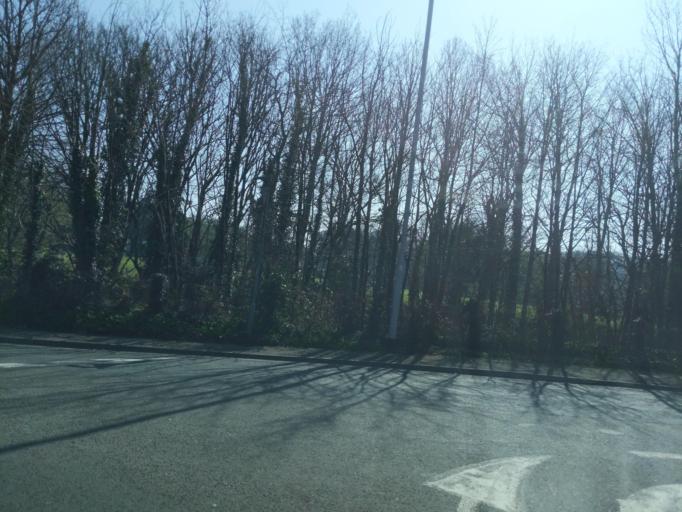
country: GB
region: England
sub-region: Devon
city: Plympton
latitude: 50.3901
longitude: -4.0588
